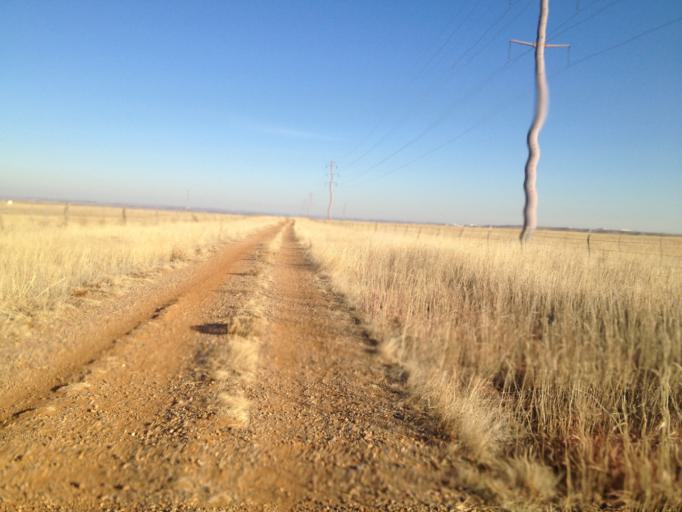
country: US
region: Colorado
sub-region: Boulder County
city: Superior
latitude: 39.9286
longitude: -105.1942
